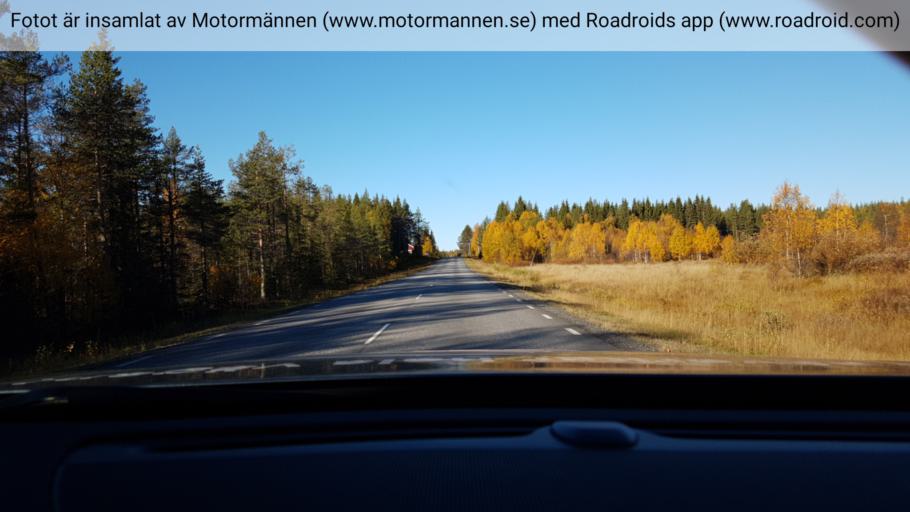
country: SE
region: Vaesterbotten
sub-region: Skelleftea Kommun
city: Storvik
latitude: 65.3364
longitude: 20.5644
